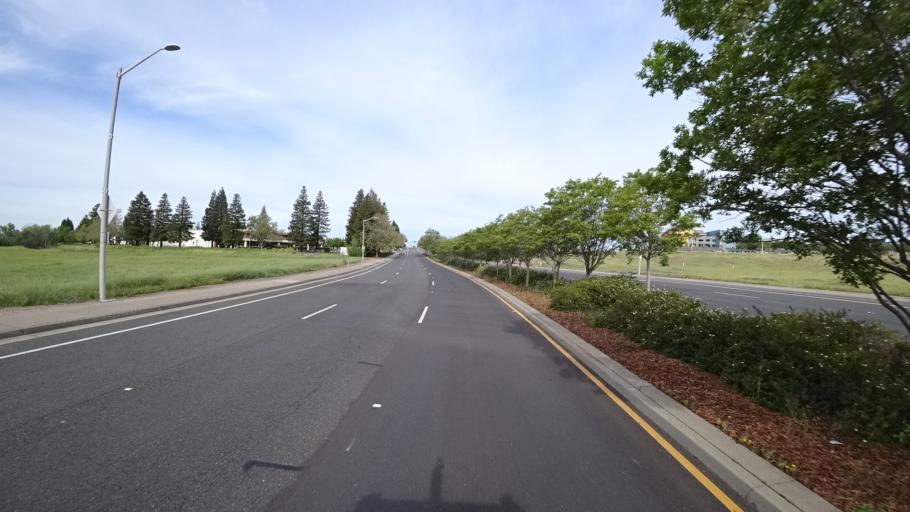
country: US
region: California
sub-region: Placer County
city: Rocklin
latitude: 38.8171
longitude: -121.2898
